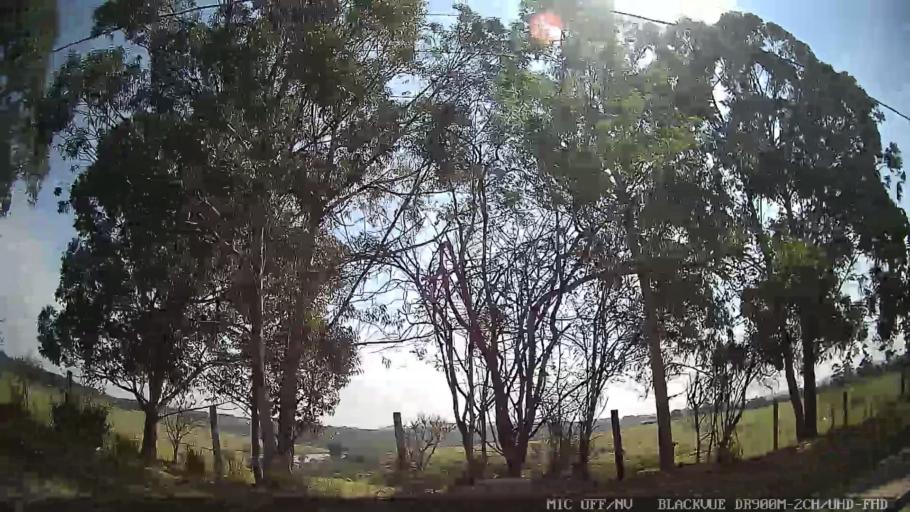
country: BR
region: Sao Paulo
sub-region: Cabreuva
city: Cabreuva
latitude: -23.2748
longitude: -47.0605
